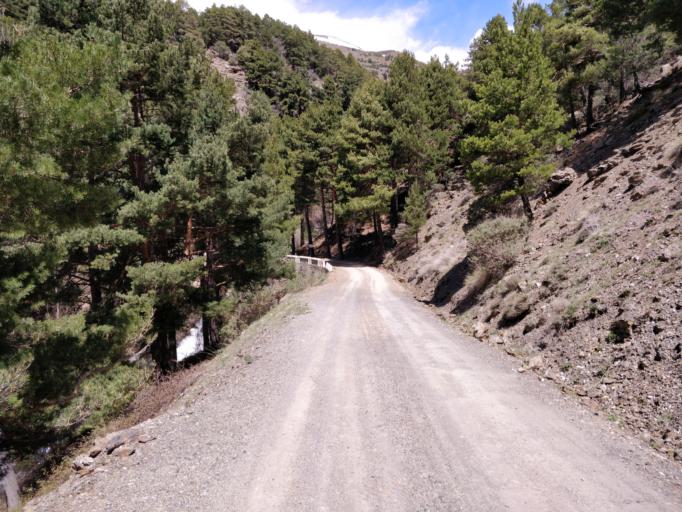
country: ES
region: Andalusia
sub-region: Provincia de Granada
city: Soportujar
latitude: 36.9681
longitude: -3.4088
